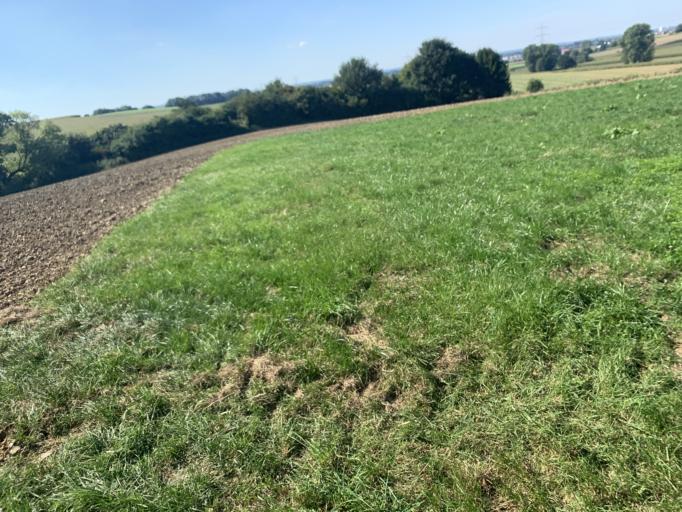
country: DE
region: Bavaria
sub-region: Swabia
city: Mering
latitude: 48.2851
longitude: 11.0040
